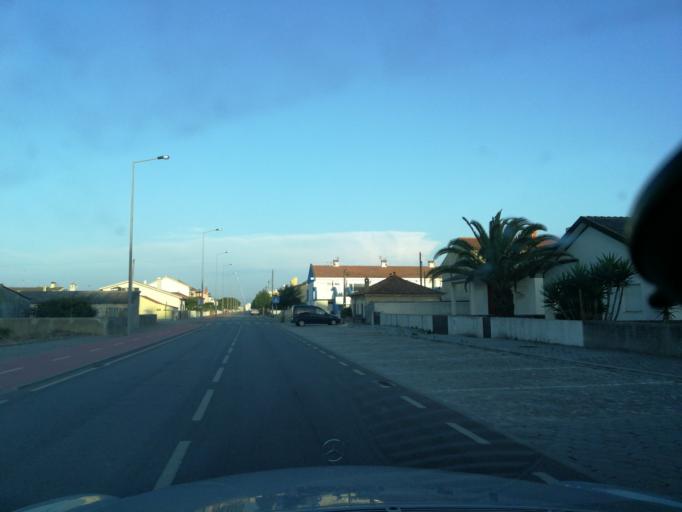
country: PT
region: Aveiro
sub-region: Murtosa
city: Murtosa
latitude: 40.7593
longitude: -8.7107
